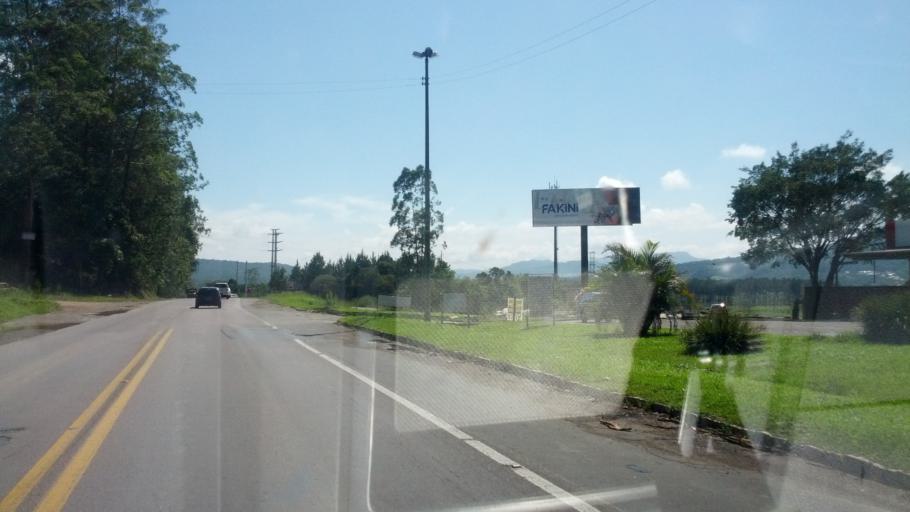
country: BR
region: Santa Catarina
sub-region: Rio Do Sul
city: Rio do Sul
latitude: -27.1866
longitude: -49.6072
